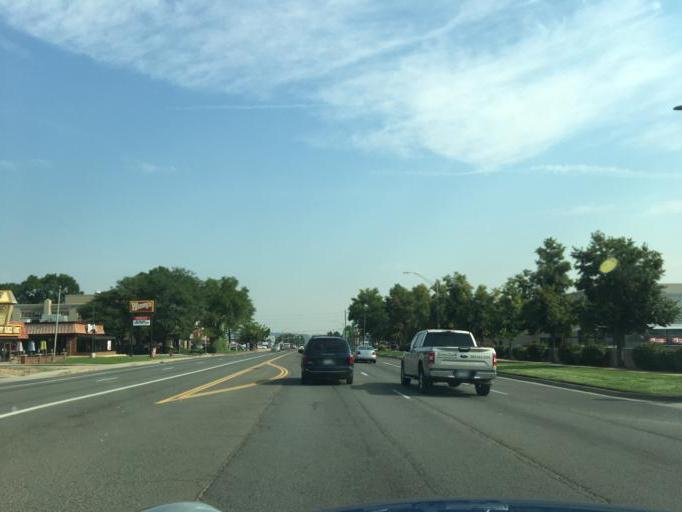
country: US
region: Colorado
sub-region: Jefferson County
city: Wheat Ridge
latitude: 39.7710
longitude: -105.0814
